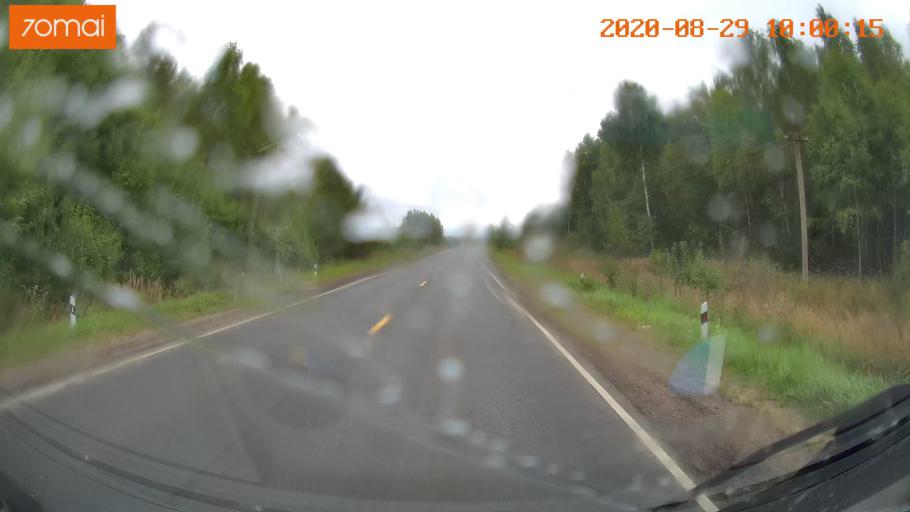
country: RU
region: Ivanovo
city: Zarechnyy
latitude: 57.4099
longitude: 42.3884
